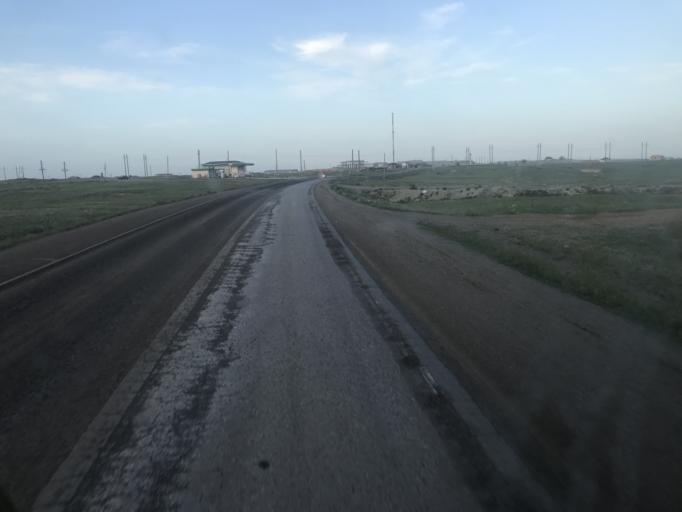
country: KZ
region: Aqtoebe
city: Khromtau
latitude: 50.2594
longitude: 58.4026
